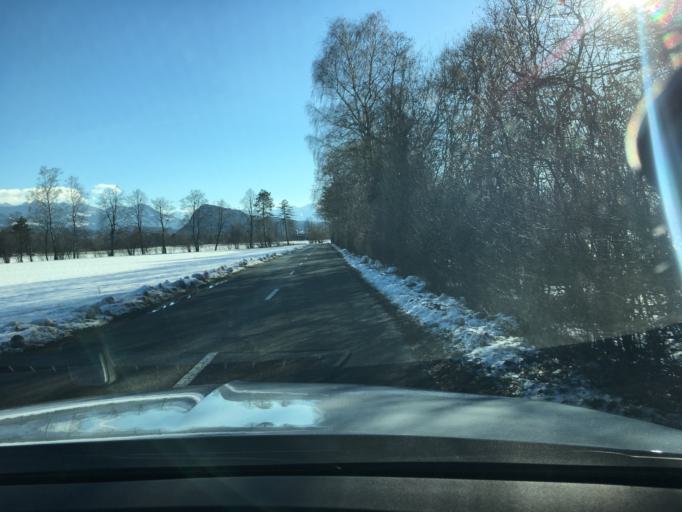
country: CH
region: Saint Gallen
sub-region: Wahlkreis Rheintal
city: Rebstein
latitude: 47.3701
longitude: 9.5924
